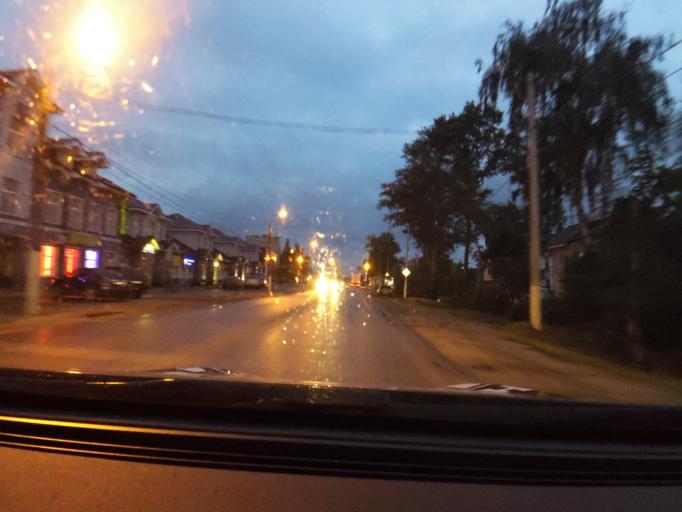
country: RU
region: Vladimir
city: Aleksandrov
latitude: 56.4030
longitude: 38.6917
